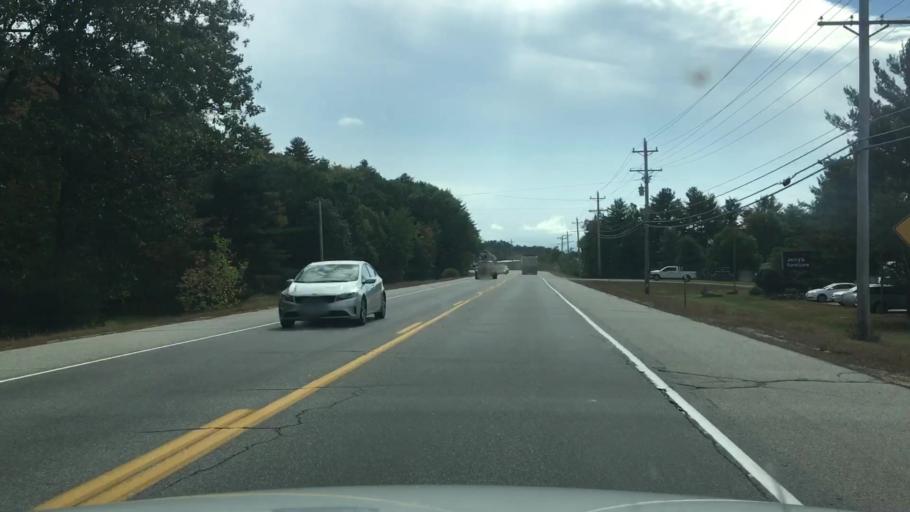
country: US
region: New Hampshire
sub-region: Carroll County
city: North Conway
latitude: 44.0904
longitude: -71.1489
